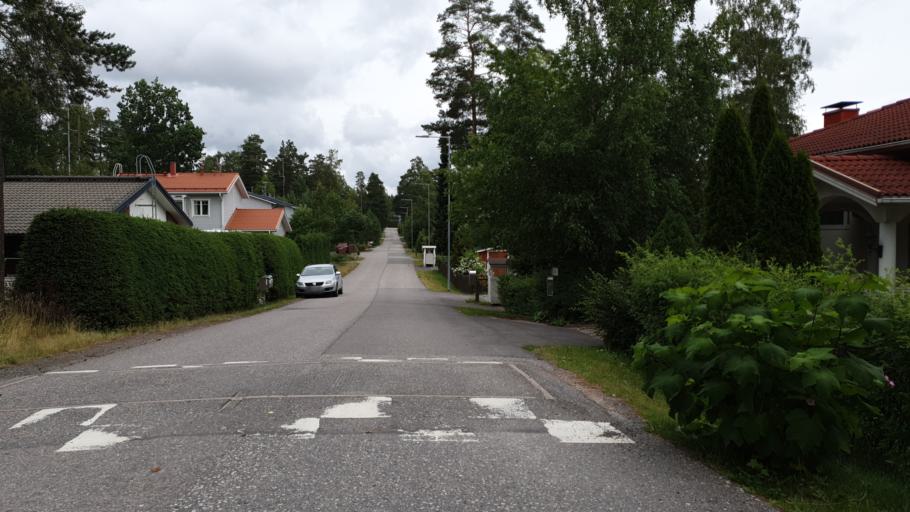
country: FI
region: Uusimaa
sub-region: Helsinki
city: Teekkarikylae
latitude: 60.2827
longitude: 24.9014
